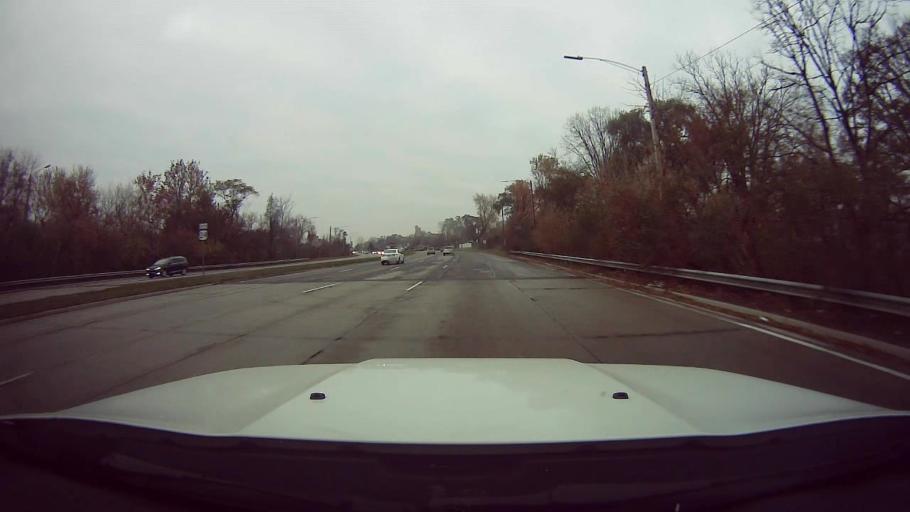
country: US
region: Michigan
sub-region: Wayne County
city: Redford
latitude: 42.4413
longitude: -83.2790
